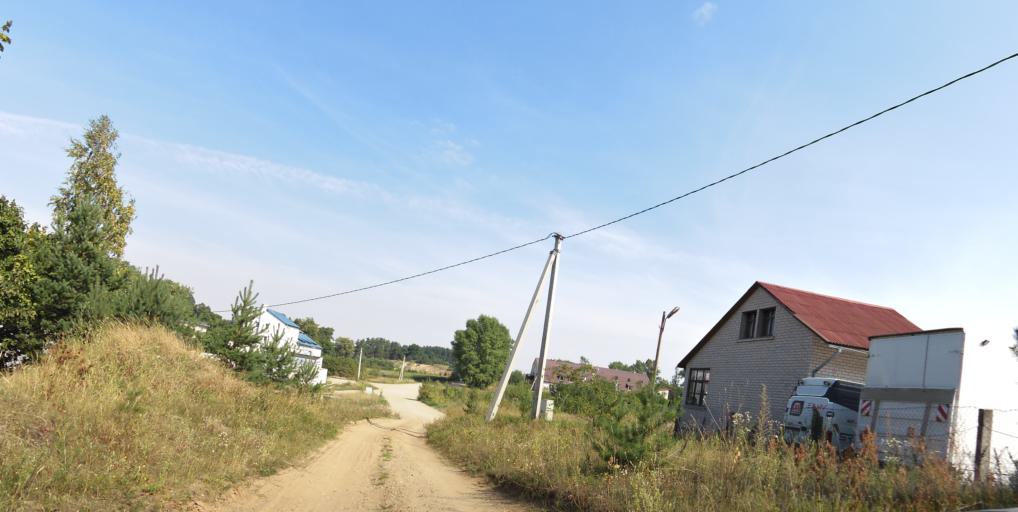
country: LT
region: Vilnius County
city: Pilaite
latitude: 54.7016
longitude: 25.1964
